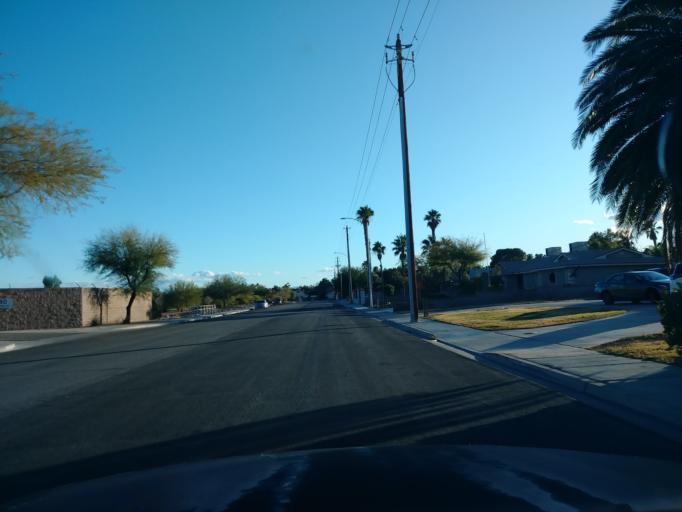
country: US
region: Nevada
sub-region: Clark County
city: Spring Valley
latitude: 36.1504
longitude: -115.2388
